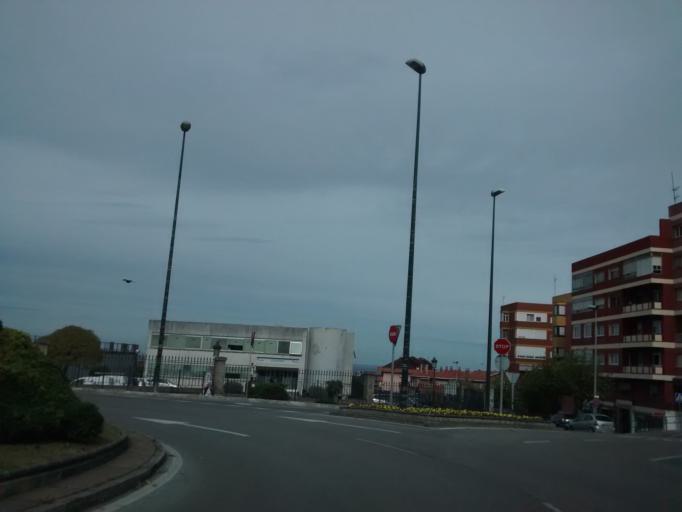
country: ES
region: Cantabria
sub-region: Provincia de Cantabria
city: Santander
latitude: 43.4611
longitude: -3.8301
